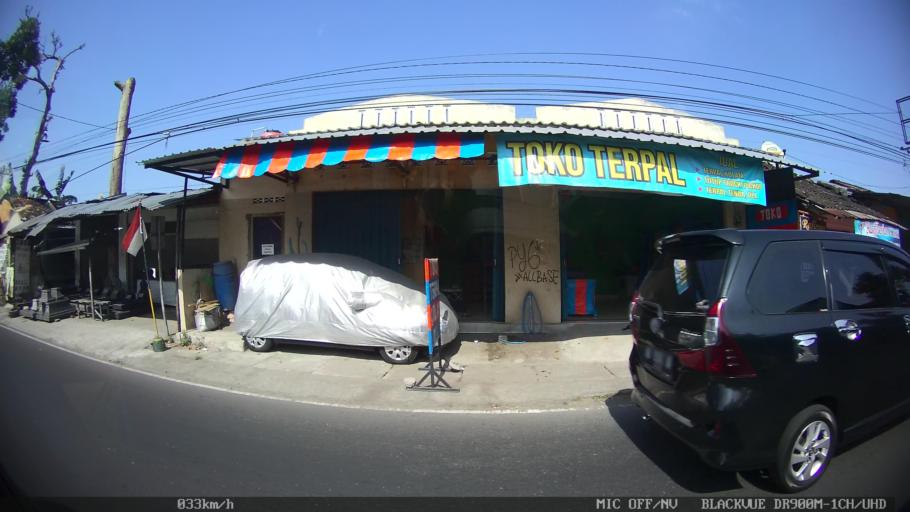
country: ID
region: Daerah Istimewa Yogyakarta
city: Sewon
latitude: -7.8768
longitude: 110.3912
